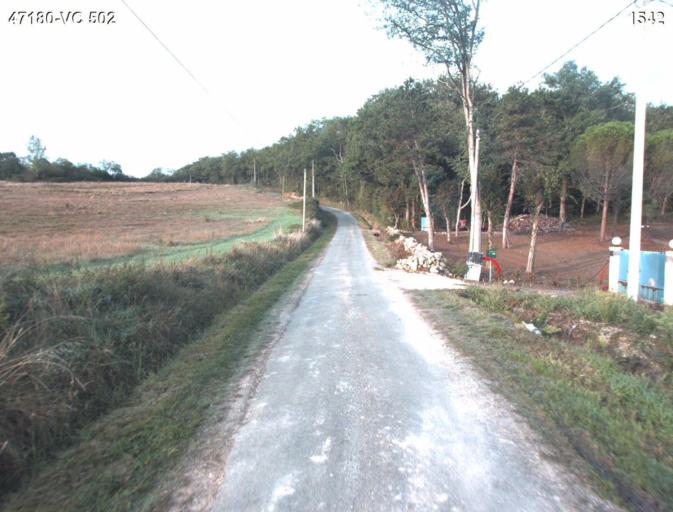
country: FR
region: Aquitaine
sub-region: Departement du Lot-et-Garonne
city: Sainte-Colombe-en-Bruilhois
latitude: 44.1709
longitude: 0.4817
